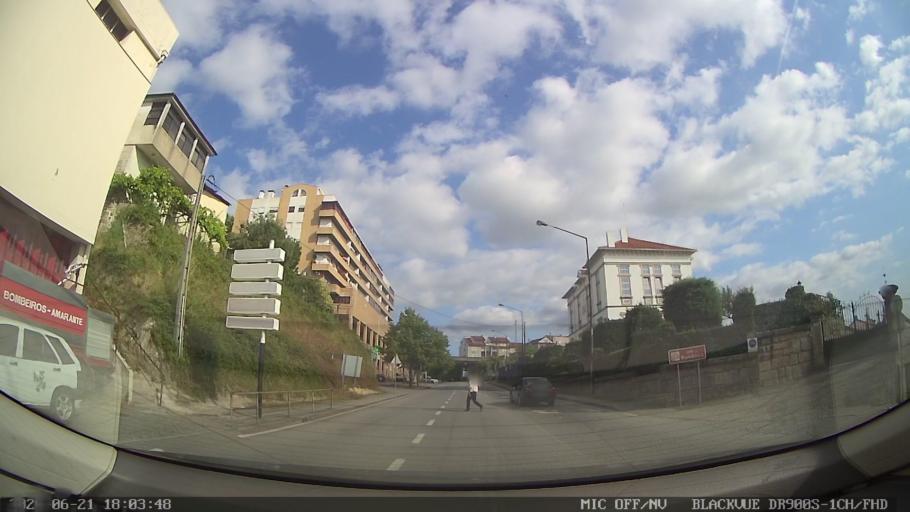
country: PT
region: Porto
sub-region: Amarante
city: Amarante
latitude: 41.2723
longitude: -8.0810
